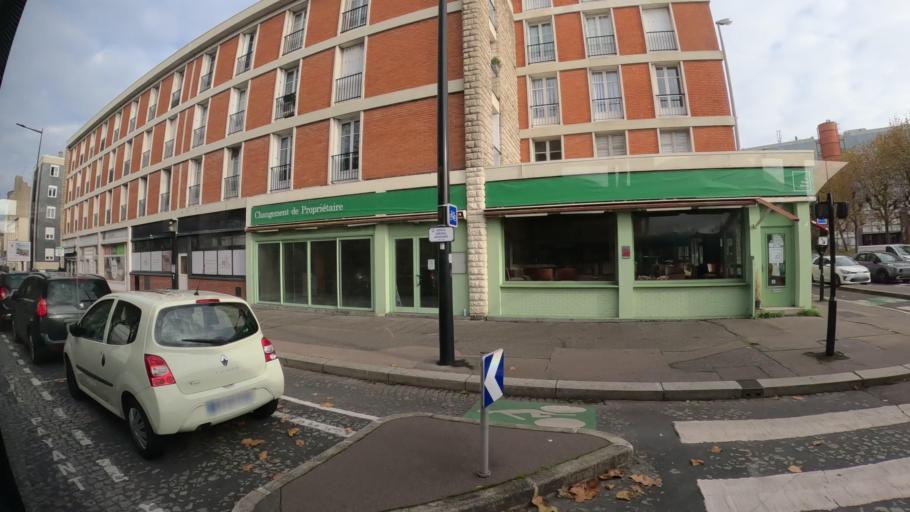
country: FR
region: Haute-Normandie
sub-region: Departement de la Seine-Maritime
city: Le Havre
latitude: 49.4909
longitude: 0.1167
